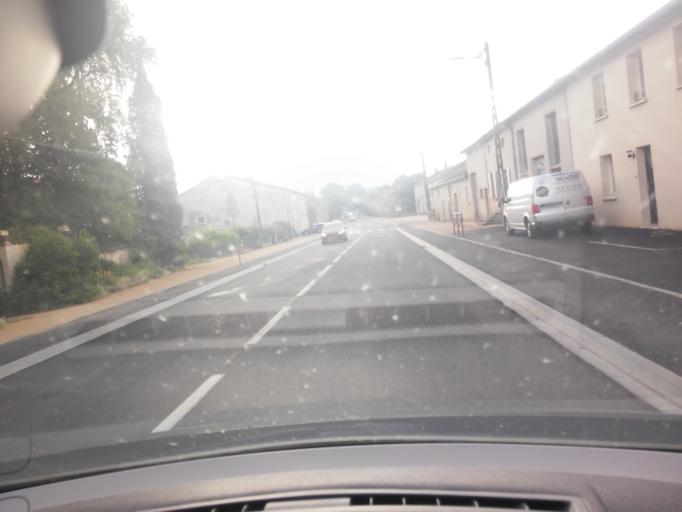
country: FR
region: Lorraine
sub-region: Departement de Meurthe-et-Moselle
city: Doncourt-les-Conflans
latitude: 49.0932
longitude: 5.9465
